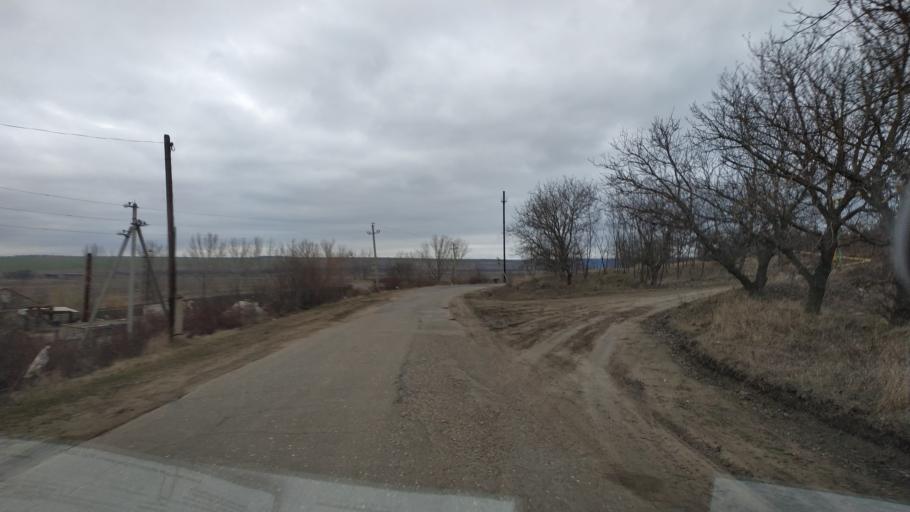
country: MD
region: Causeni
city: Causeni
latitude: 46.6666
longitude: 29.4566
